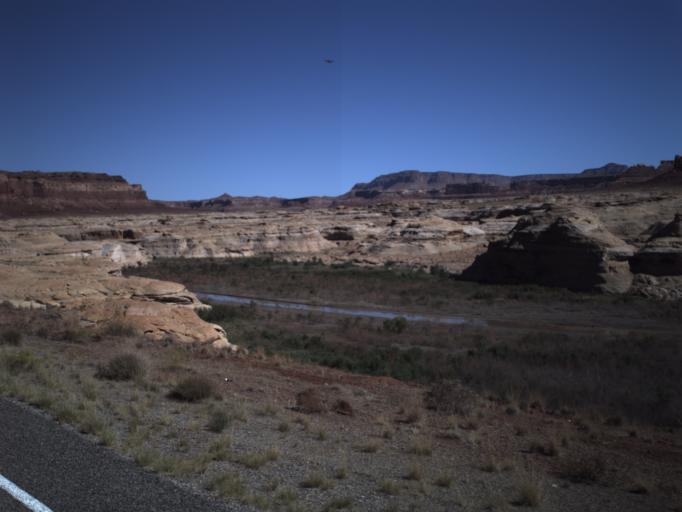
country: US
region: Utah
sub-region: San Juan County
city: Blanding
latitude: 37.8982
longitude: -110.3985
